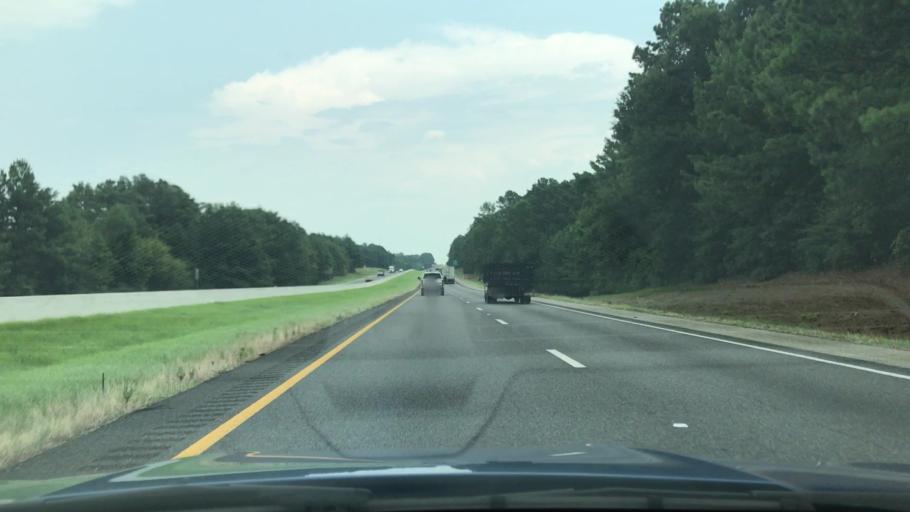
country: US
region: Texas
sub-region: Gregg County
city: Liberty City
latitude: 32.4357
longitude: -94.9696
